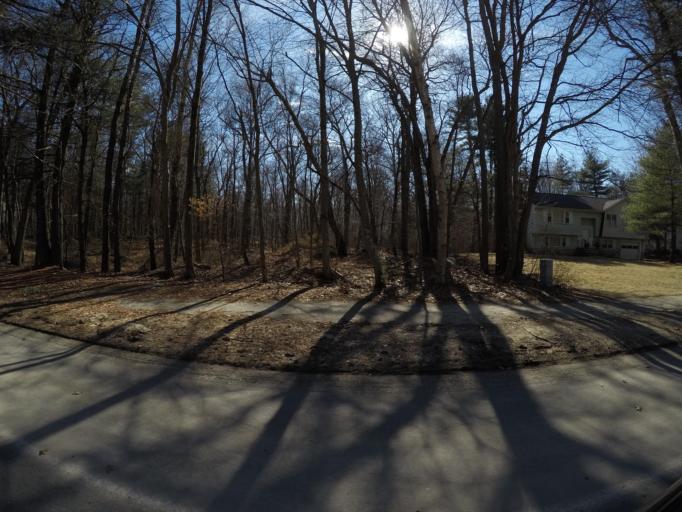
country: US
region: Massachusetts
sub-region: Norfolk County
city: Sharon
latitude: 42.0963
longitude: -71.1557
